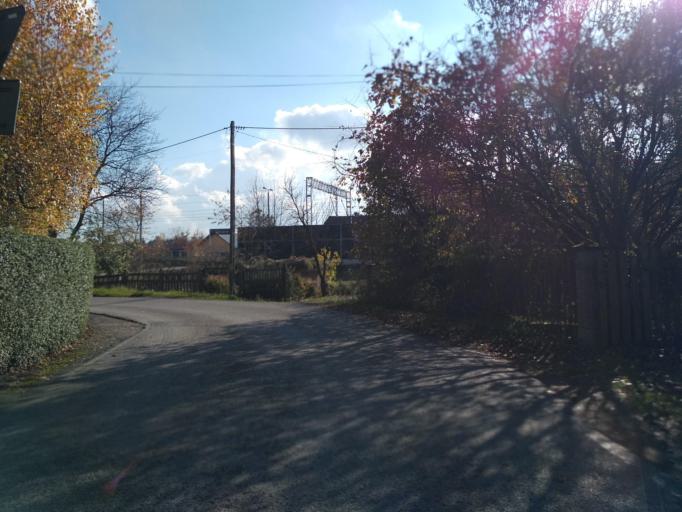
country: PL
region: Subcarpathian Voivodeship
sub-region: Powiat rzeszowski
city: Trzciana
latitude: 50.0793
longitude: 21.8390
